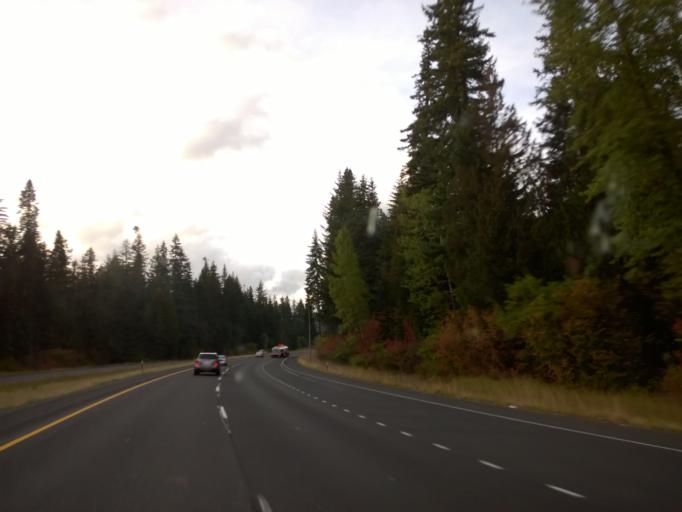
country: US
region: Washington
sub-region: Kittitas County
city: Cle Elum
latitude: 47.3093
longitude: -121.3118
